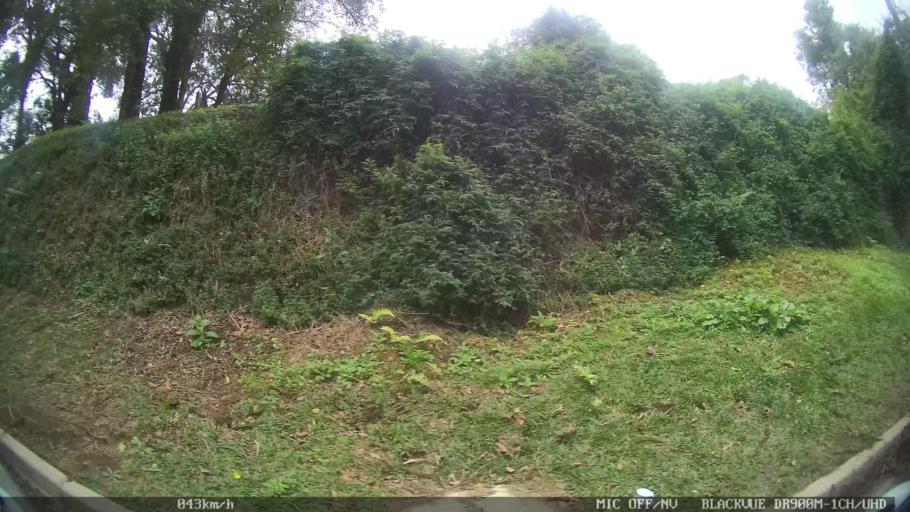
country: BR
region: Parana
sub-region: Colombo
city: Colombo
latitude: -25.3494
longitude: -49.2270
